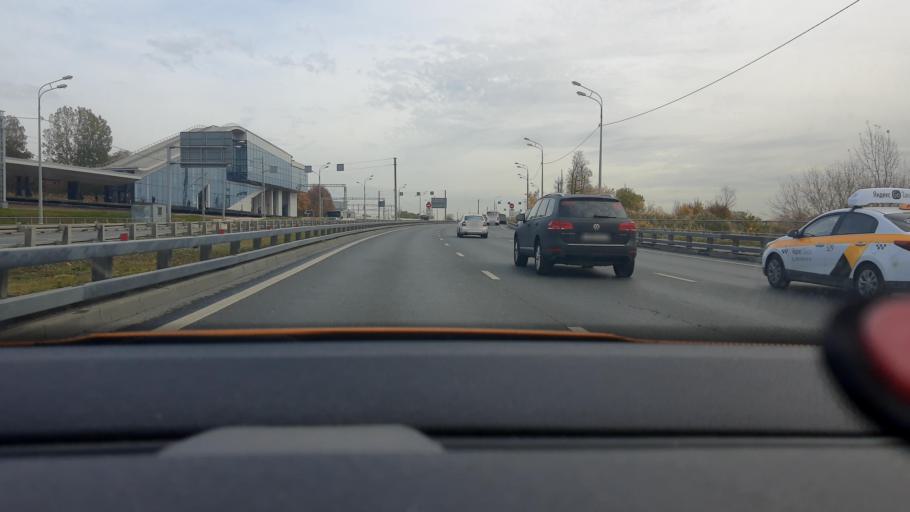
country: RU
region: Moscow
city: Strogino
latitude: 55.8309
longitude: 37.3820
